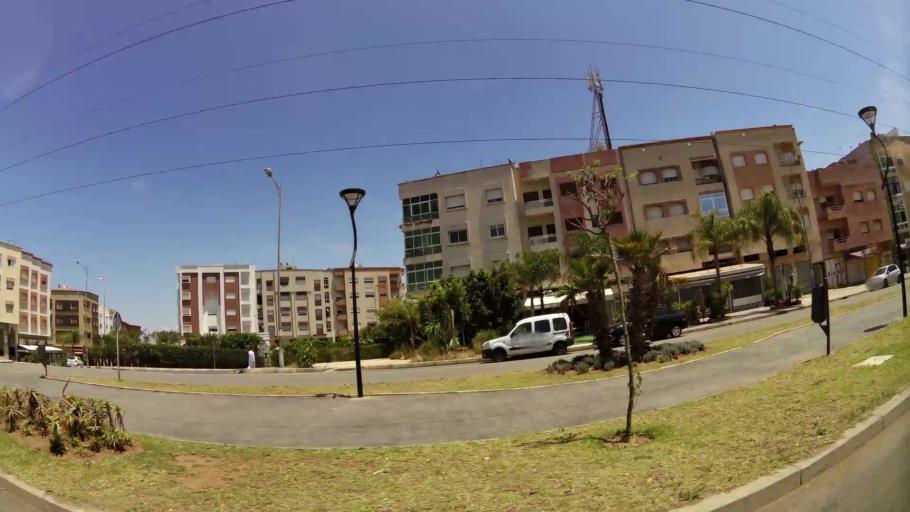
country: MA
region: Gharb-Chrarda-Beni Hssen
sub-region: Kenitra Province
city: Kenitra
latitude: 34.2549
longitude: -6.6152
